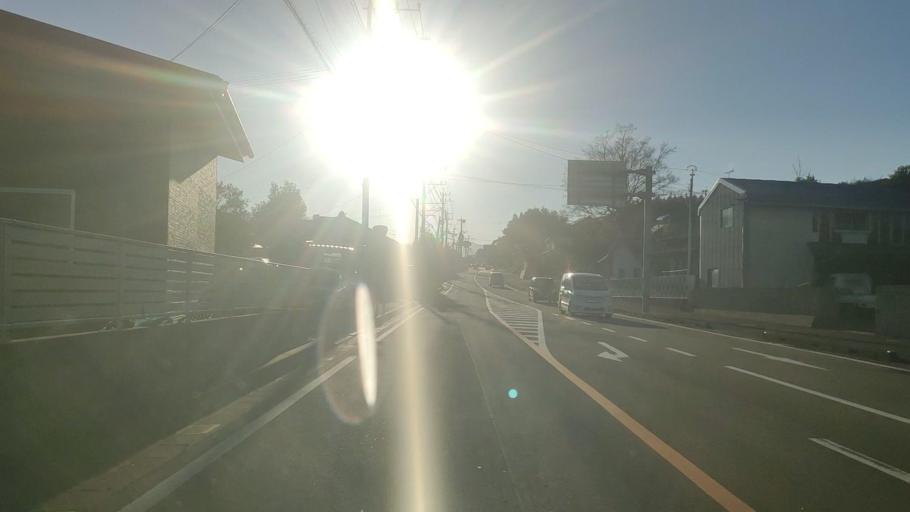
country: JP
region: Miyazaki
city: Miyazaki-shi
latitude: 31.8472
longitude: 131.3485
